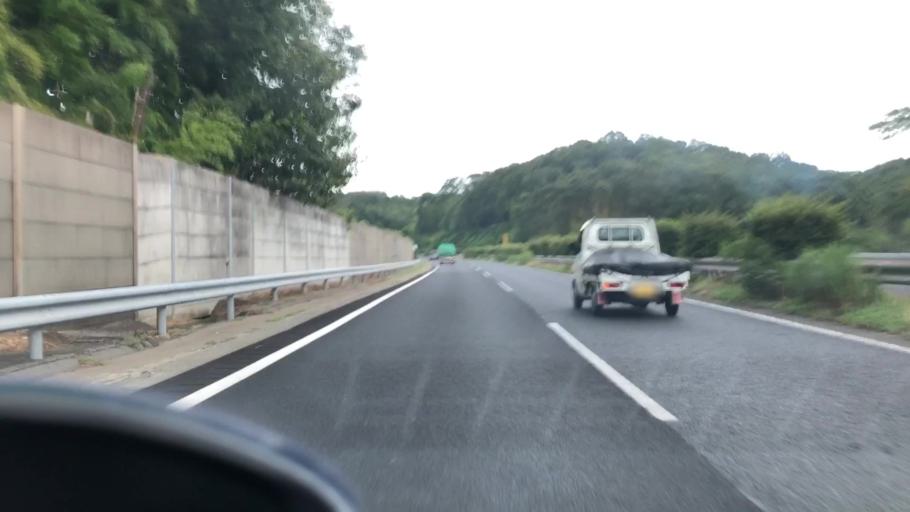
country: JP
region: Hyogo
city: Yashiro
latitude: 34.9122
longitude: 135.0410
